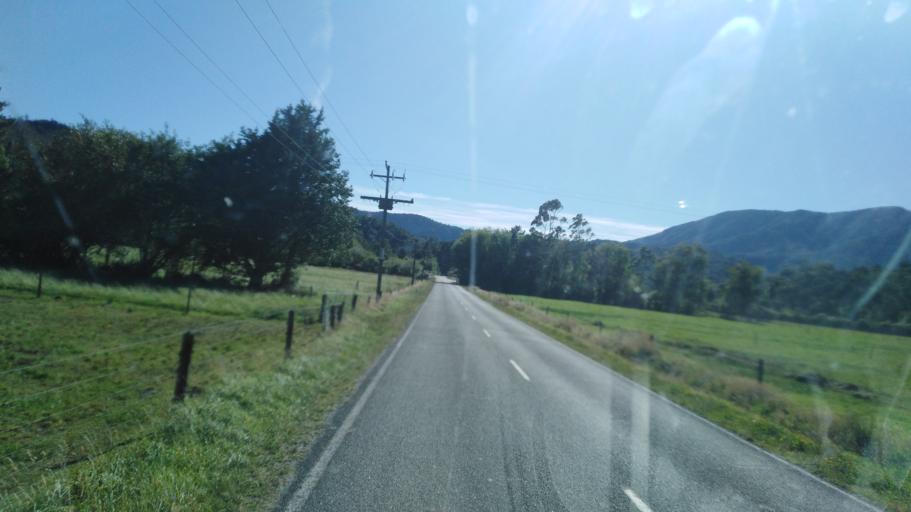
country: NZ
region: West Coast
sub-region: Buller District
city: Westport
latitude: -41.5318
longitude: 171.9633
